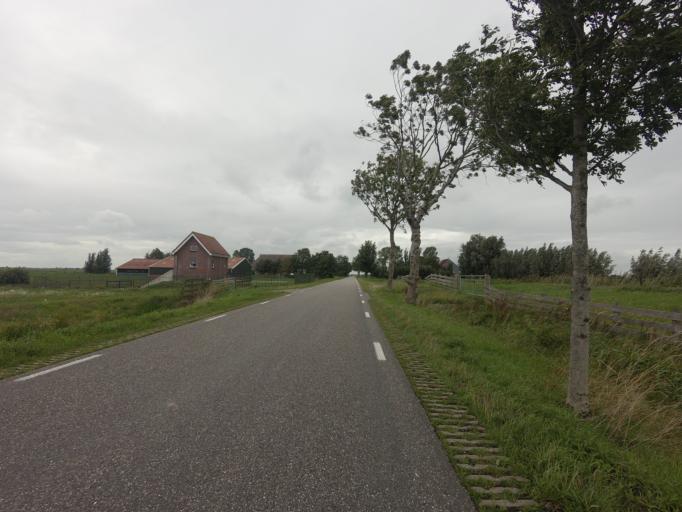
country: NL
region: Friesland
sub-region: Sudwest Fryslan
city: Heeg
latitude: 52.9679
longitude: 5.5691
